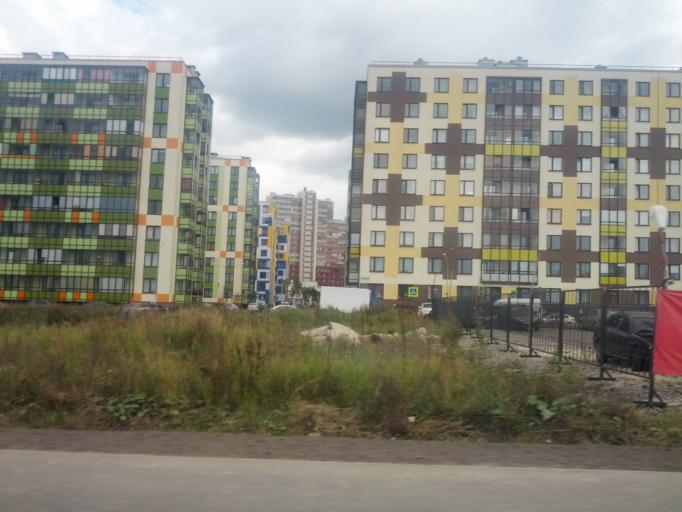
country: RU
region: Leningrad
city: Rybatskoye
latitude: 59.8982
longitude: 30.5048
